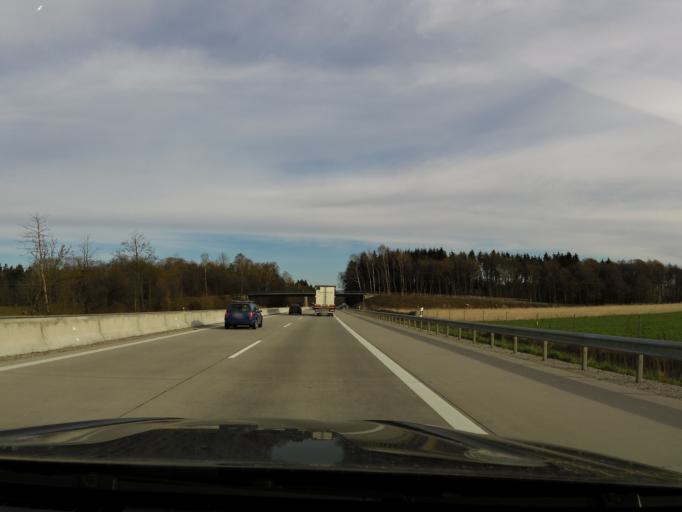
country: DE
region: Bavaria
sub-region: Upper Bavaria
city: Raubling
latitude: 47.7756
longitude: 12.0952
